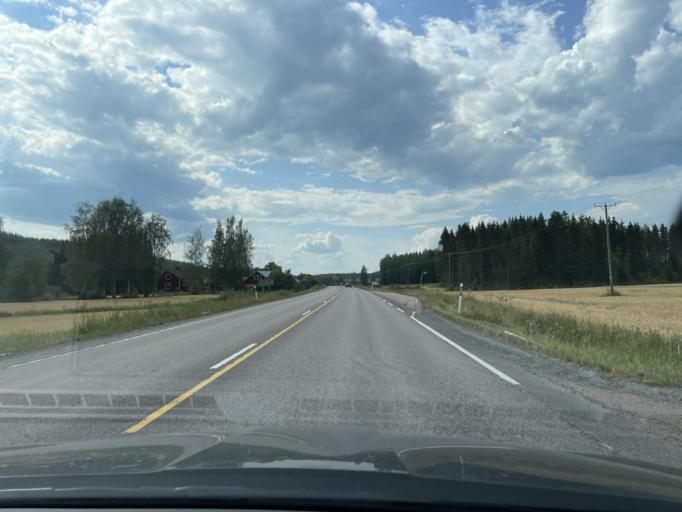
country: FI
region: Central Finland
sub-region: Jyvaeskylae
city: Korpilahti
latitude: 61.9920
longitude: 25.4508
